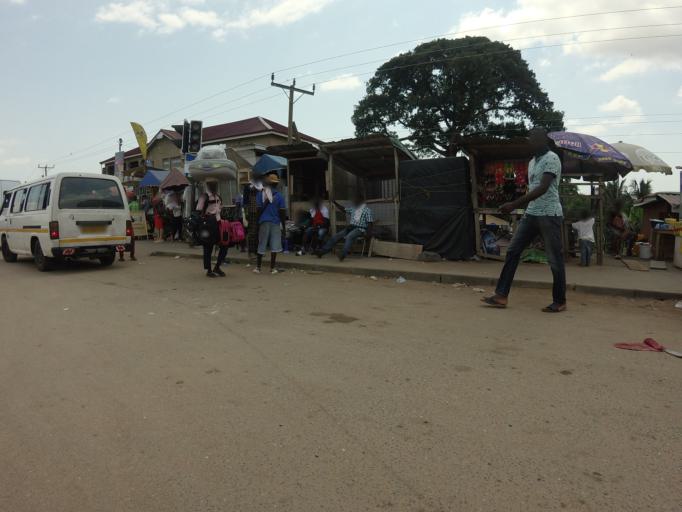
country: GH
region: Greater Accra
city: Gbawe
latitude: 5.6273
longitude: -0.3120
